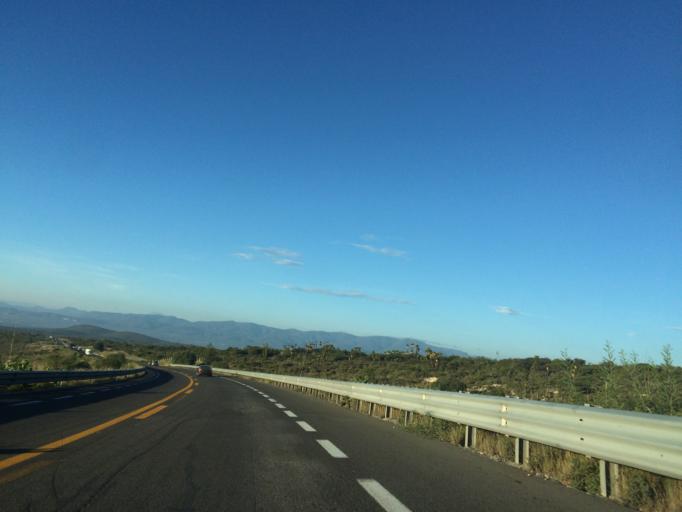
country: MX
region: Puebla
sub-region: Tehuacan
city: Magdalena Cuayucatepec
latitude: 18.6143
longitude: -97.4757
